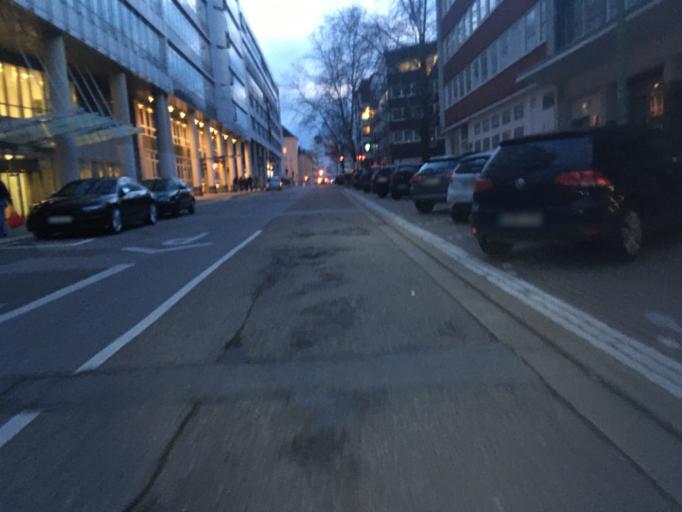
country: DE
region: North Rhine-Westphalia
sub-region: Regierungsbezirk Dusseldorf
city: Essen
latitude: 51.4491
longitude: 7.0134
